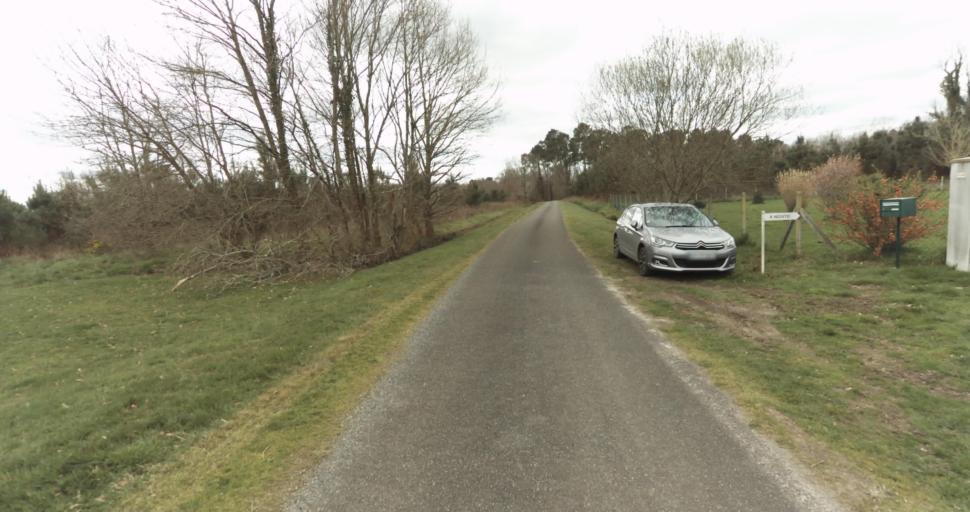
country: FR
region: Aquitaine
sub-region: Departement des Landes
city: Roquefort
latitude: 44.0793
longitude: -0.3889
